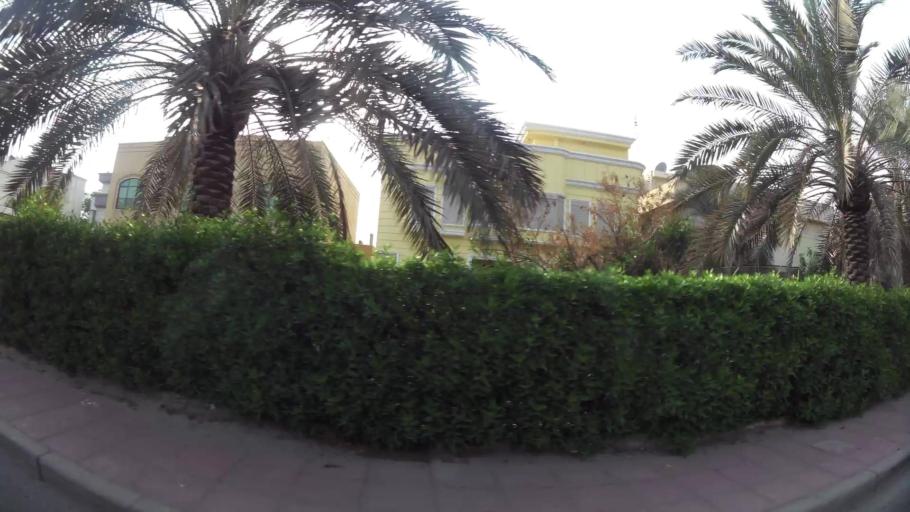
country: KW
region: Mubarak al Kabir
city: Sabah as Salim
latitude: 29.2231
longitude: 48.0608
